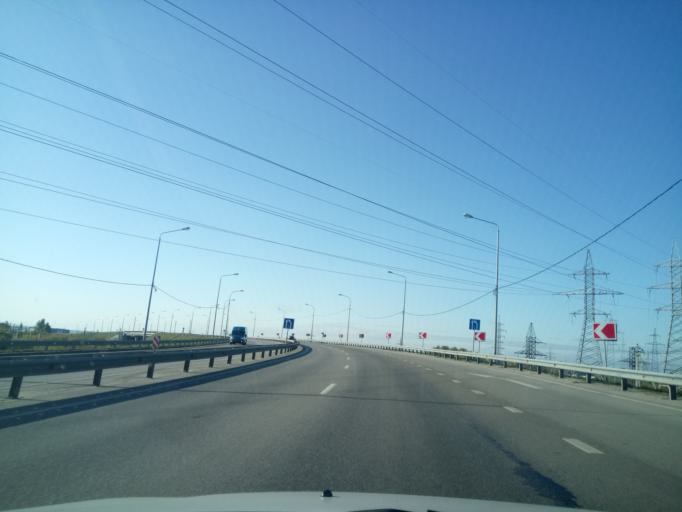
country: RU
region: Nizjnij Novgorod
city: Burevestnik
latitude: 56.1813
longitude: 43.9147
